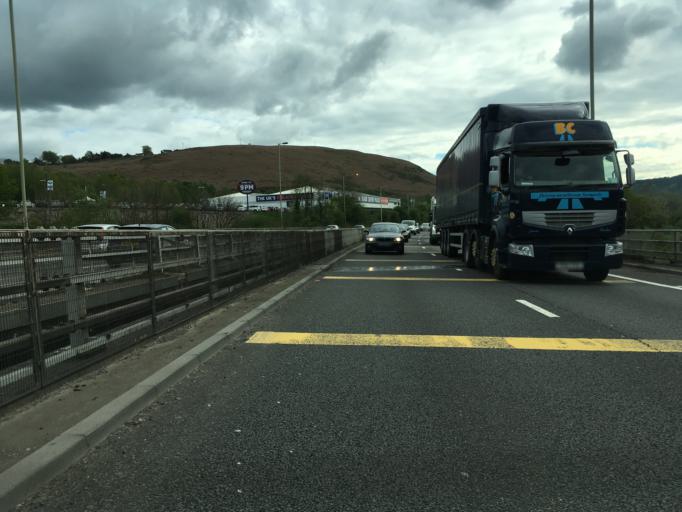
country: GB
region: Wales
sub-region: Merthyr Tydfil County Borough
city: Treharris
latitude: 51.6482
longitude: -3.3181
